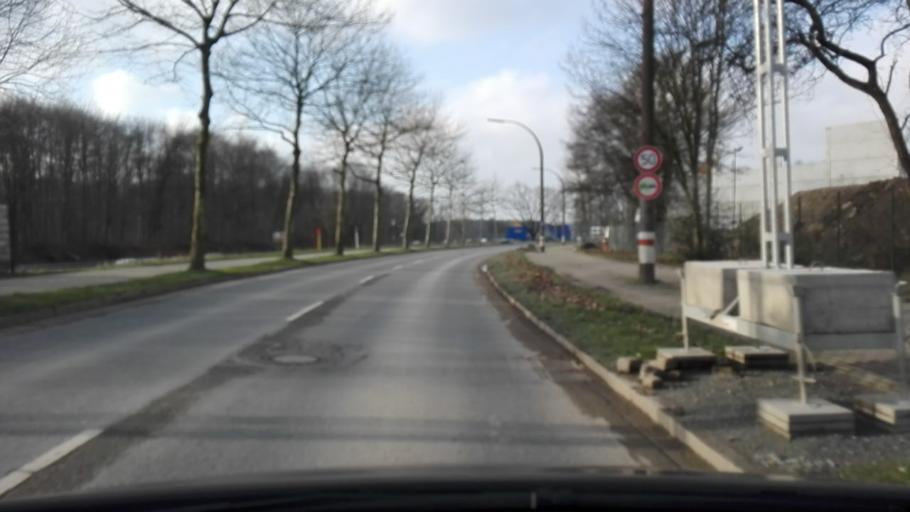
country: DE
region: North Rhine-Westphalia
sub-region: Regierungsbezirk Arnsberg
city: Dortmund
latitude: 51.4818
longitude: 7.4783
